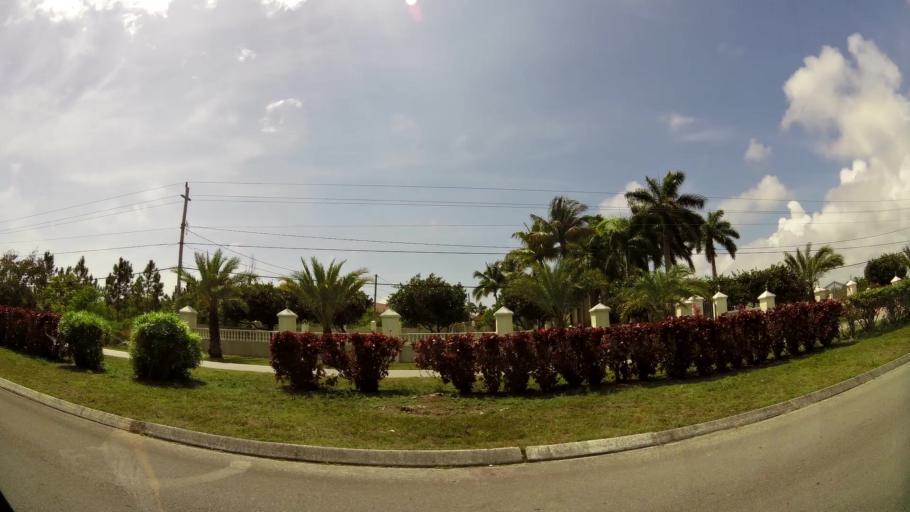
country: BS
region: Freeport
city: Freeport
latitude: 26.5071
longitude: -78.6976
